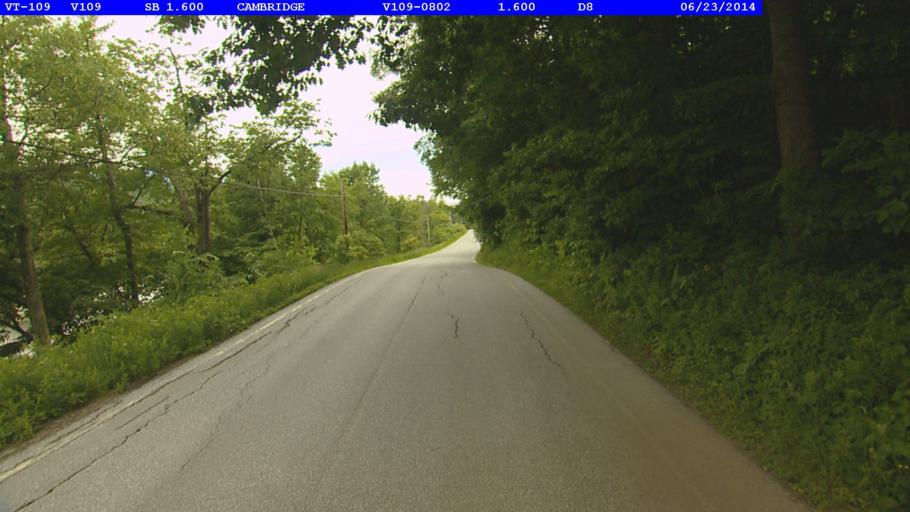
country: US
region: Vermont
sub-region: Lamoille County
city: Johnson
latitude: 44.6632
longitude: -72.8042
